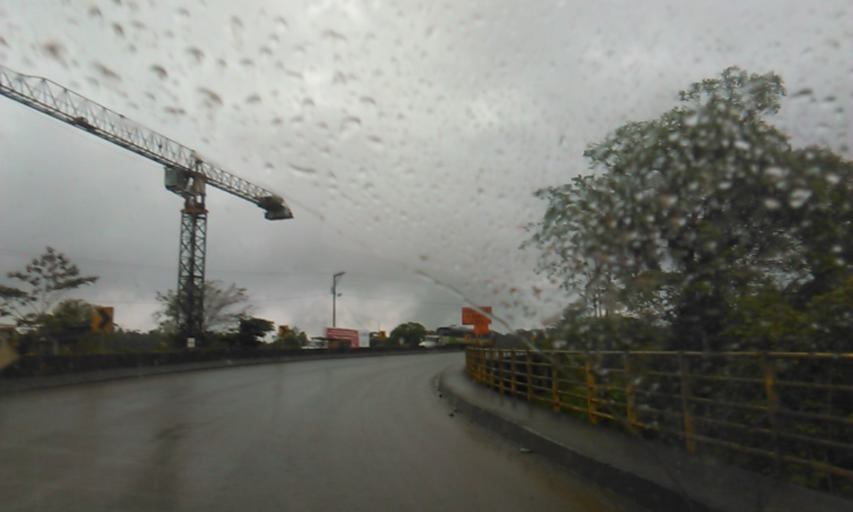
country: CO
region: Valle del Cauca
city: Buenaventura
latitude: 3.8786
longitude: -76.8921
